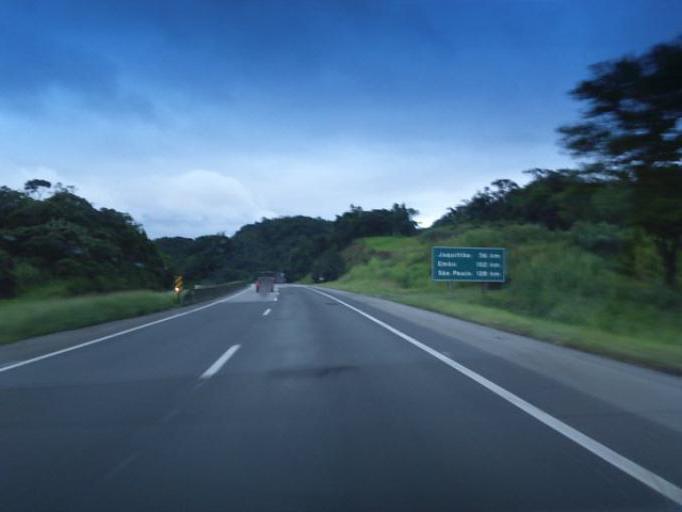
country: BR
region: Sao Paulo
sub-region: Miracatu
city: Miracatu
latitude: -24.2421
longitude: -47.3637
